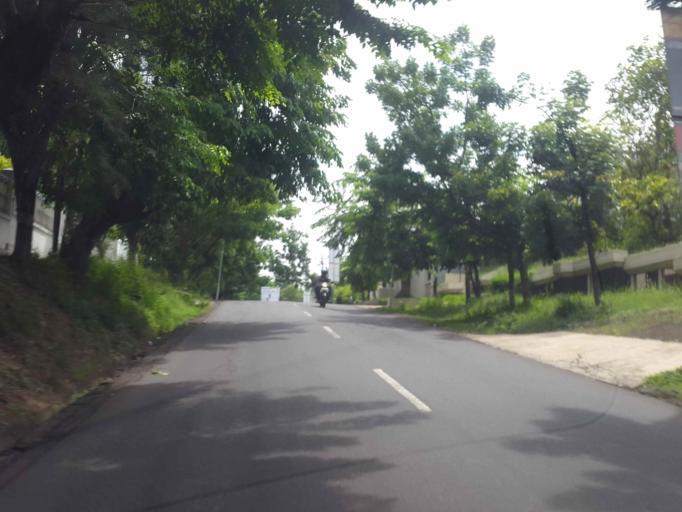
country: ID
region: Central Java
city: Semarang
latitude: -7.0041
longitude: 110.4169
